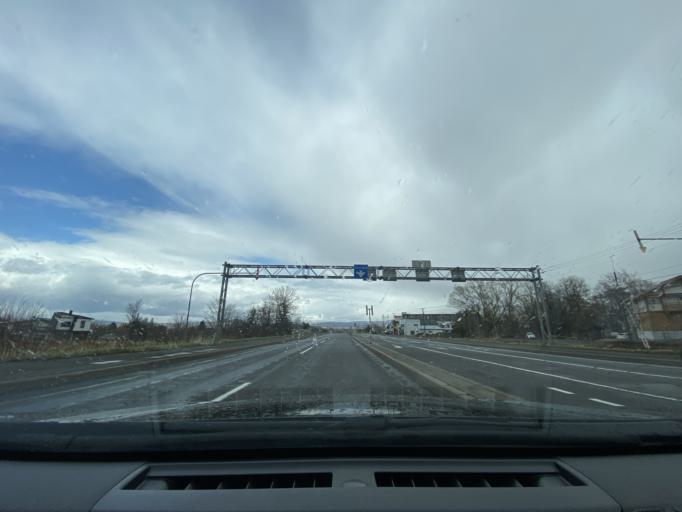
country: JP
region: Hokkaido
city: Fukagawa
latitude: 43.6905
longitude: 142.0542
